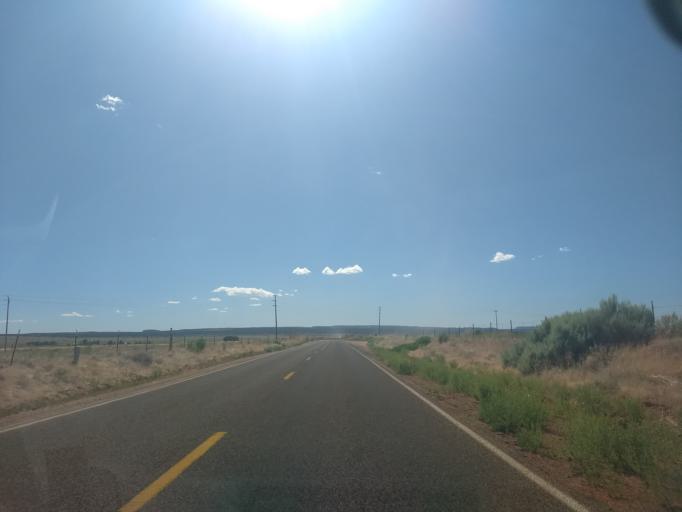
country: US
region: Arizona
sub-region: Mohave County
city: Colorado City
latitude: 36.9469
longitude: -112.9538
